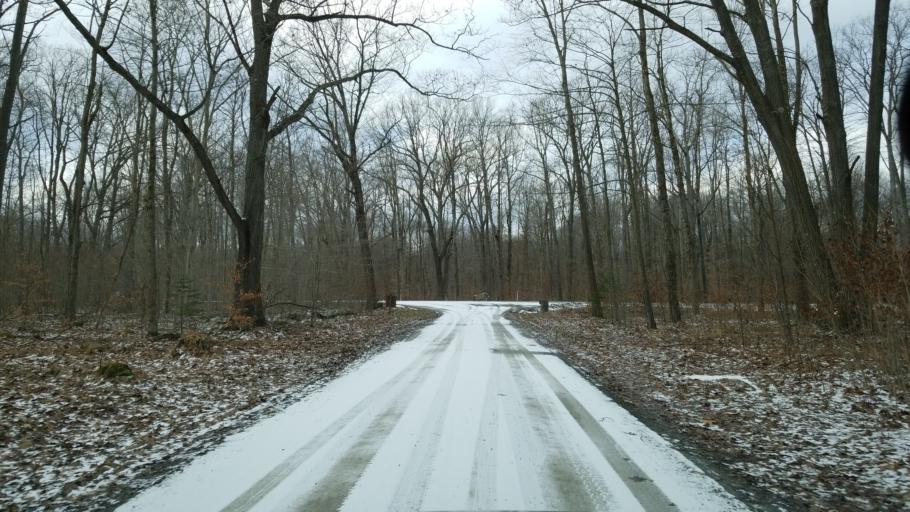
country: US
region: Pennsylvania
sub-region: Clearfield County
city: Clearfield
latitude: 41.1379
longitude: -78.5163
